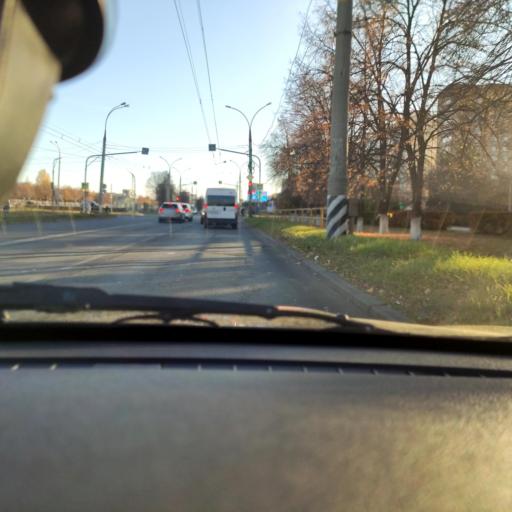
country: RU
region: Samara
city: Tol'yatti
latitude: 53.5163
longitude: 49.2730
